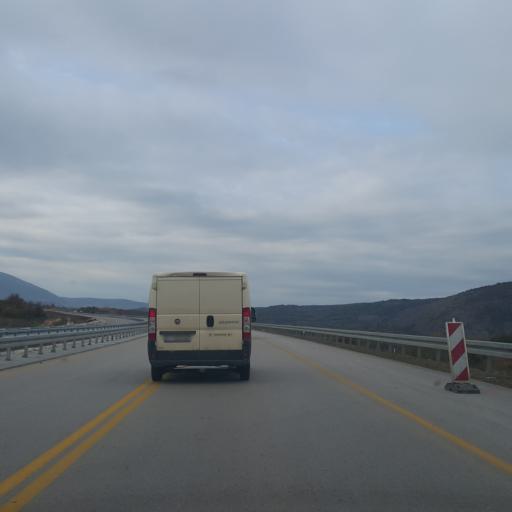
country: RS
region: Central Serbia
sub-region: Pirotski Okrug
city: Bela Palanka
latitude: 43.2241
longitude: 22.4022
